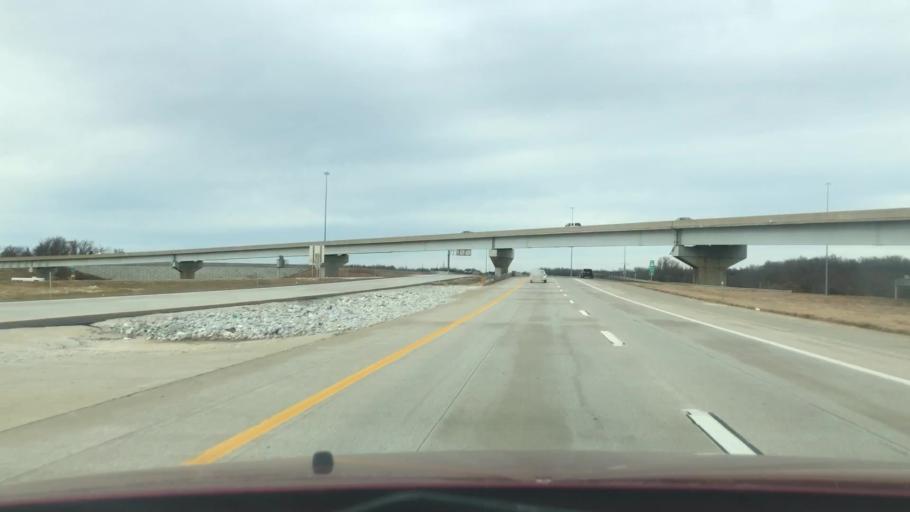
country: US
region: Missouri
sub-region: Greene County
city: Springfield
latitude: 37.2483
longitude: -93.2246
